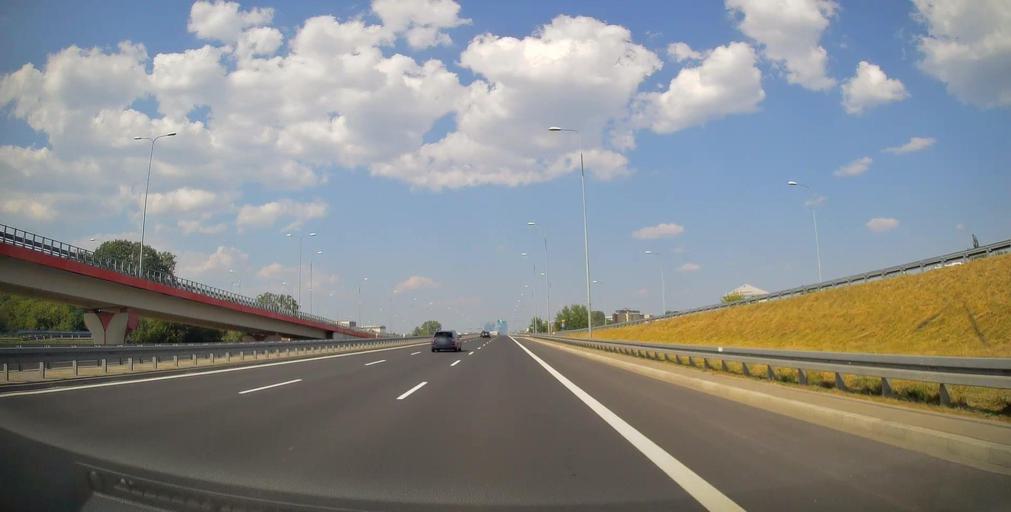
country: PL
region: Masovian Voivodeship
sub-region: Warszawa
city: Wlochy
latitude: 52.1685
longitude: 20.9862
